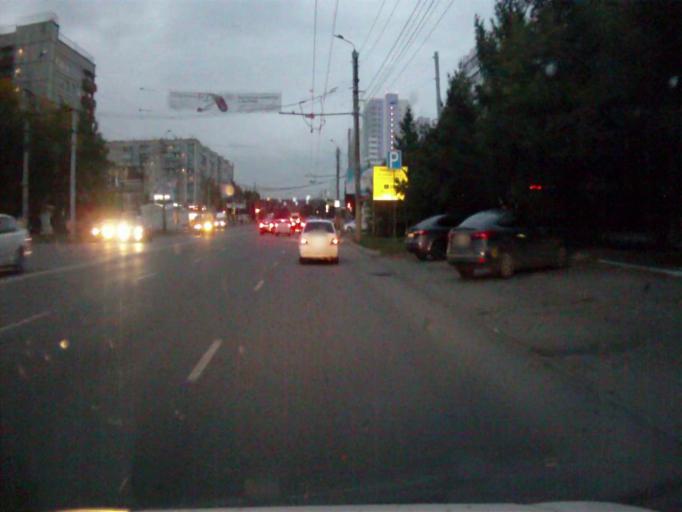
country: RU
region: Chelyabinsk
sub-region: Gorod Chelyabinsk
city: Chelyabinsk
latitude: 55.1804
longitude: 61.3326
